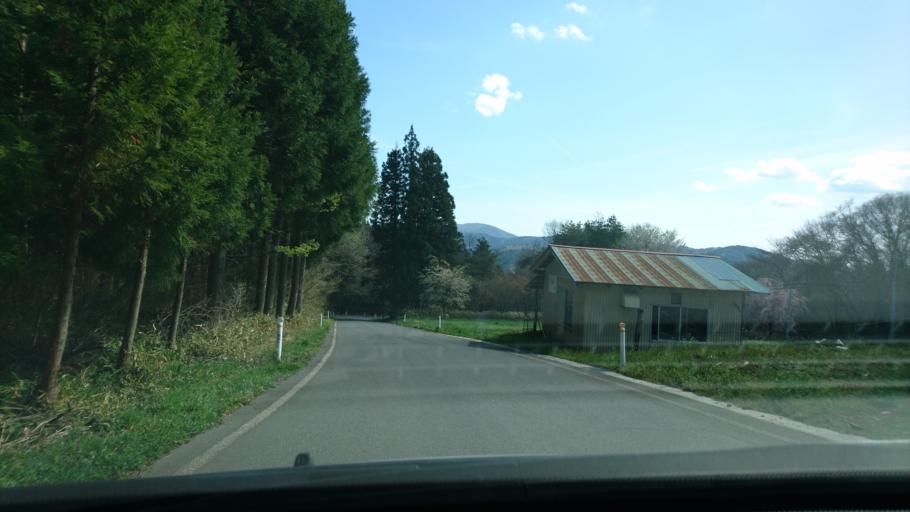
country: JP
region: Iwate
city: Ofunato
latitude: 38.9557
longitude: 141.4520
